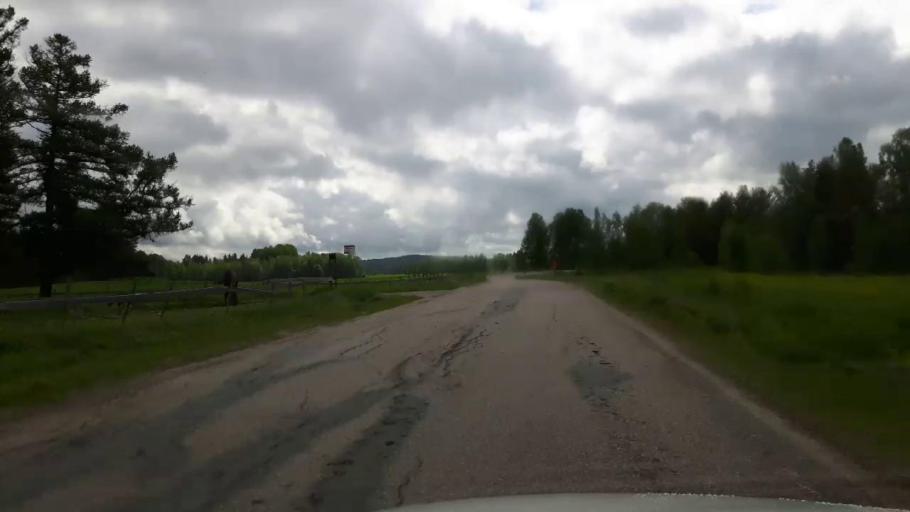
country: SE
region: Gaevleborg
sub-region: Ovanakers Kommun
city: Edsbyn
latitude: 61.3533
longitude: 15.9159
